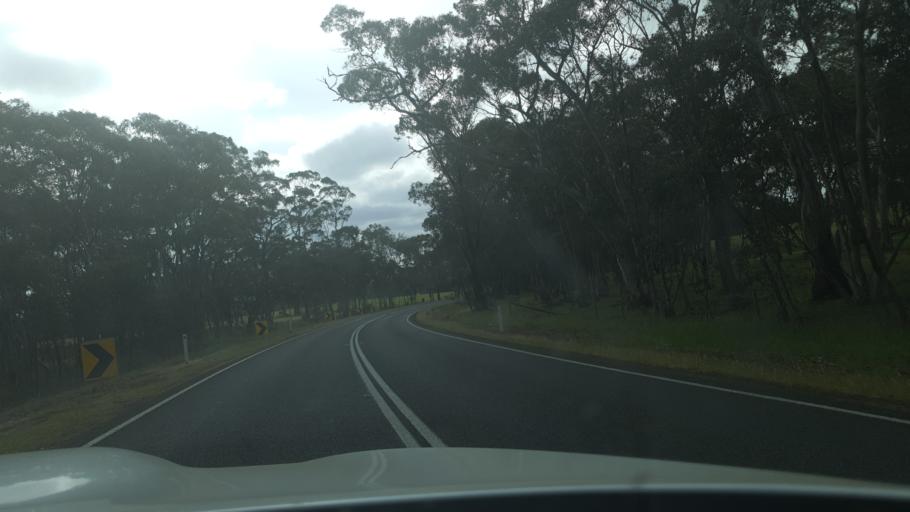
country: AU
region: Victoria
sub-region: Central Goldfields
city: Maryborough
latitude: -37.2033
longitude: 143.7083
